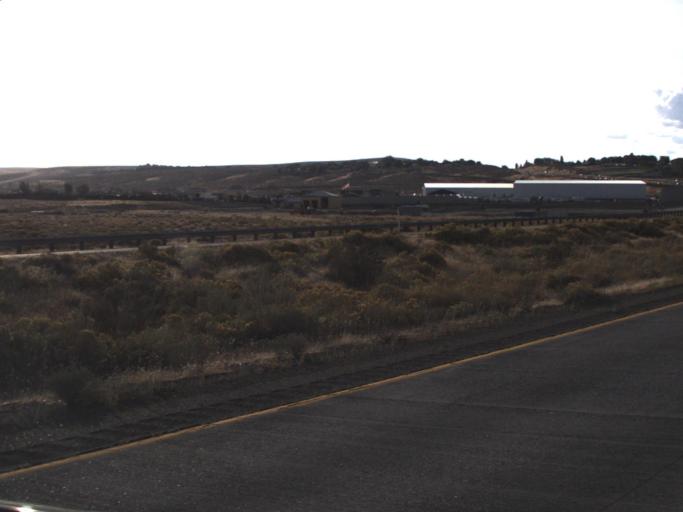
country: US
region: Washington
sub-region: Benton County
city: Richland
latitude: 46.1953
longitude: -119.2702
